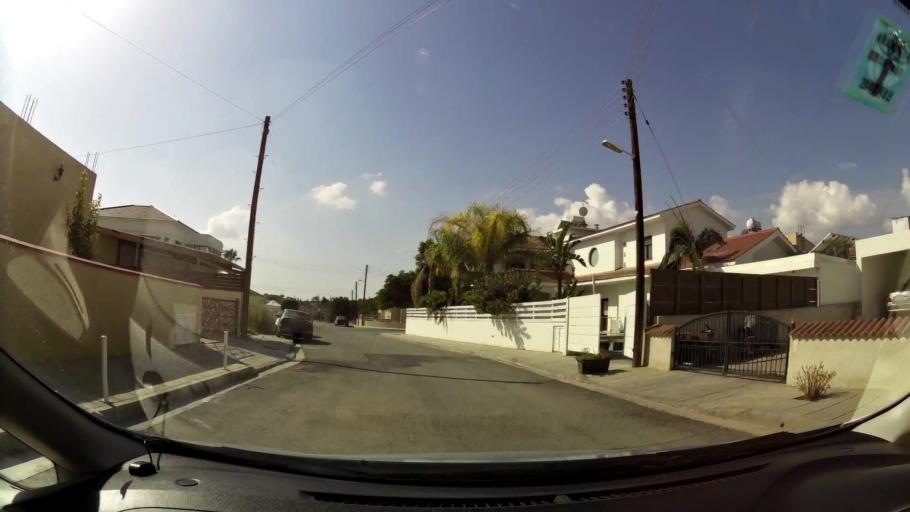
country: CY
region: Larnaka
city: Aradippou
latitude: 34.9494
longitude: 33.5769
